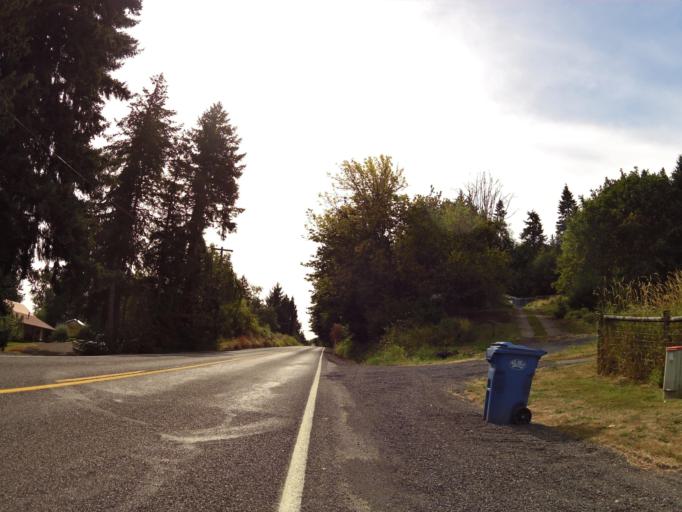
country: US
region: Washington
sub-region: Lewis County
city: Chehalis
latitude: 46.6342
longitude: -122.9707
